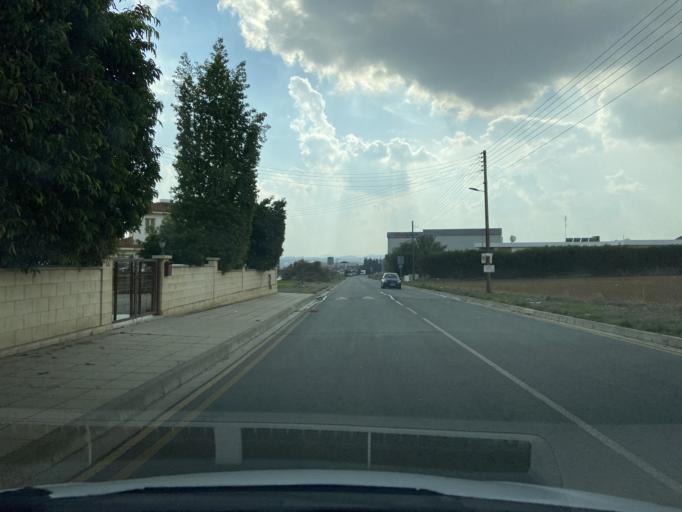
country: CY
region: Lefkosia
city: Dali
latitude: 35.0611
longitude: 33.3958
